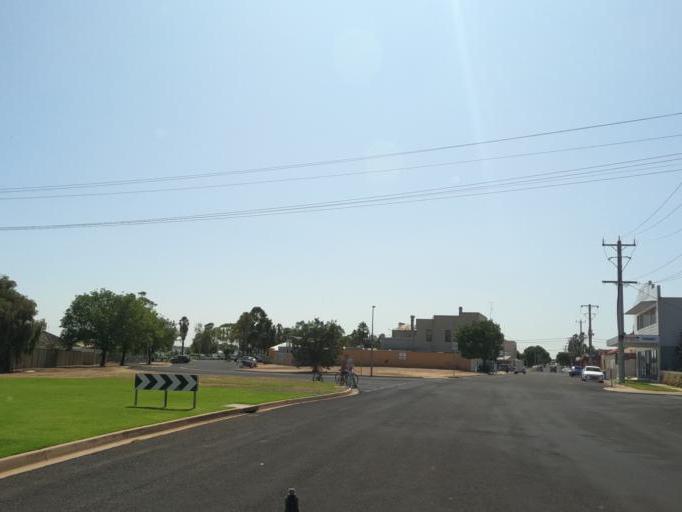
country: AU
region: Victoria
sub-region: Moira
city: Yarrawonga
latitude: -36.0091
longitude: 146.0027
